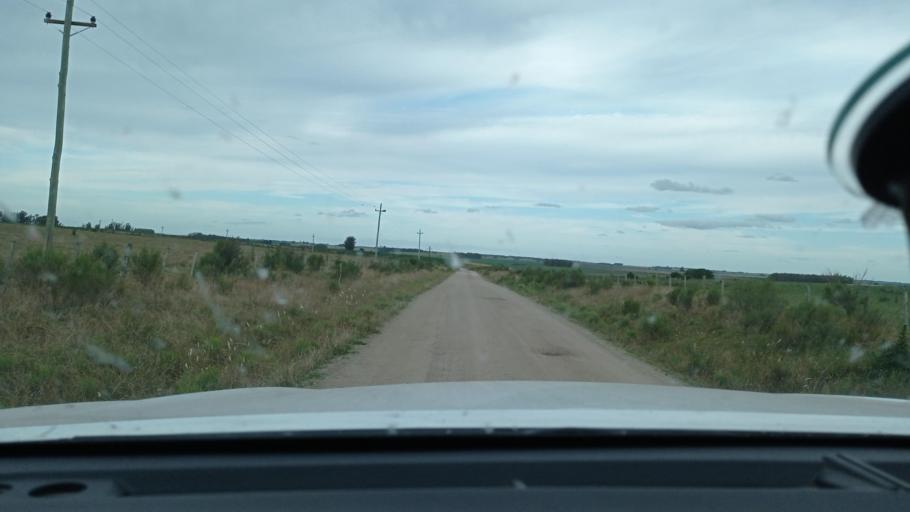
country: UY
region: Florida
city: Casupa
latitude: -34.1042
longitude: -55.7597
